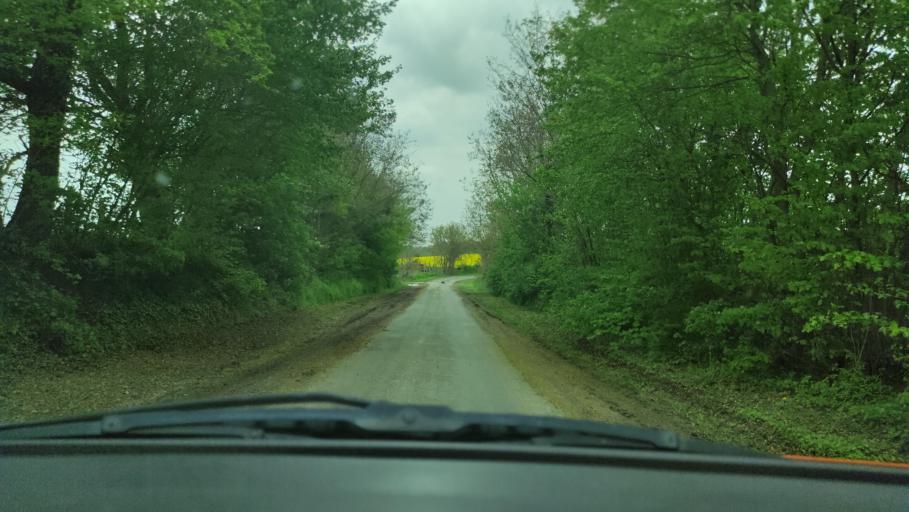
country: HU
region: Somogy
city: Taszar
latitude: 46.2976
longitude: 17.9664
